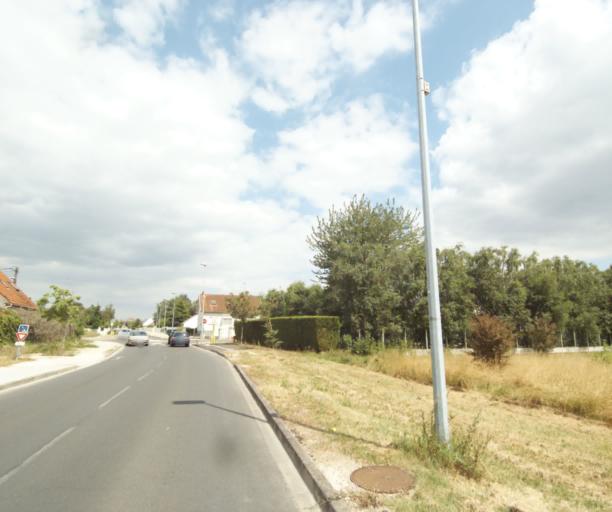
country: FR
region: Centre
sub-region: Departement du Loiret
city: Saint-Jean-de-la-Ruelle
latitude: 47.9299
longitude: 1.8538
